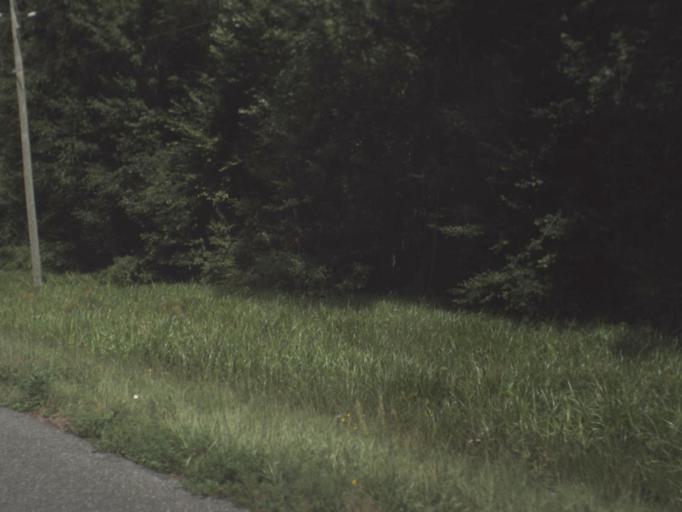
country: US
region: Florida
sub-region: Lafayette County
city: Mayo
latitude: 29.9633
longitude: -83.2317
